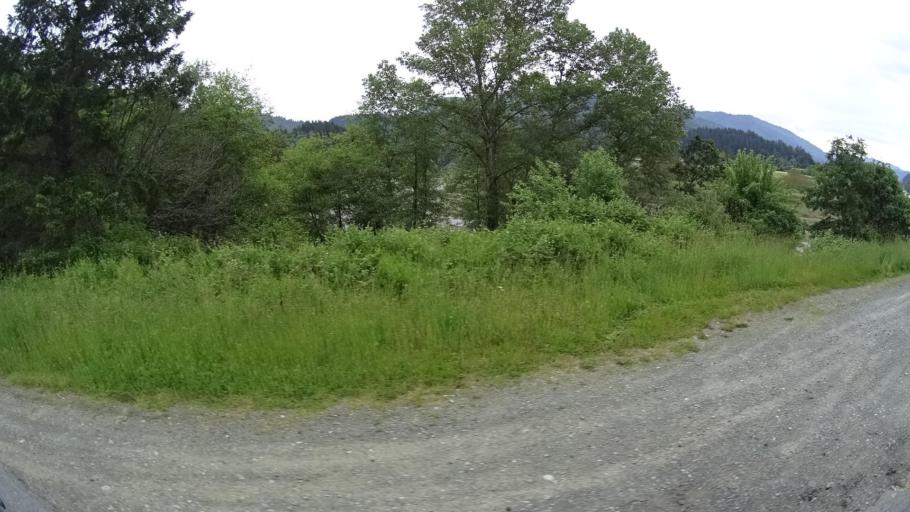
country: US
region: California
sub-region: Humboldt County
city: Willow Creek
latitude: 41.1008
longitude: -123.7111
